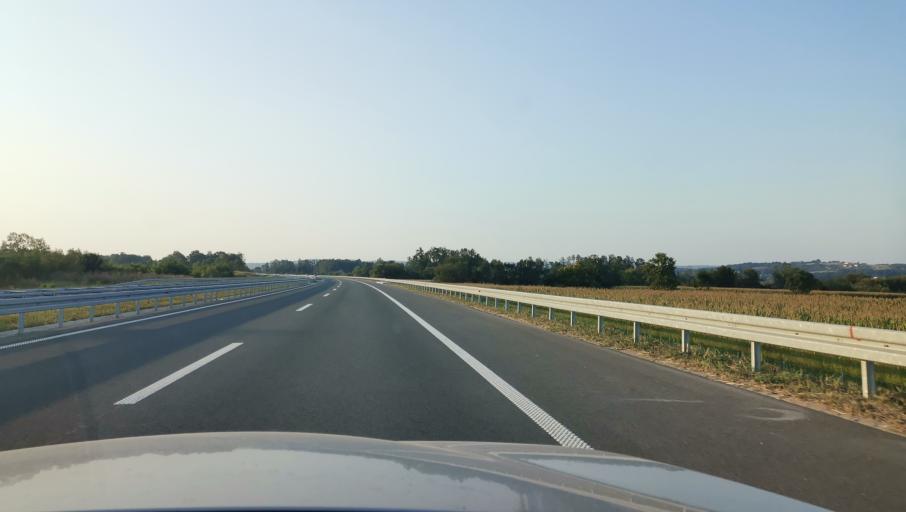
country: RS
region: Central Serbia
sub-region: Kolubarski Okrug
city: Ljig
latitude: 44.2618
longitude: 20.2711
